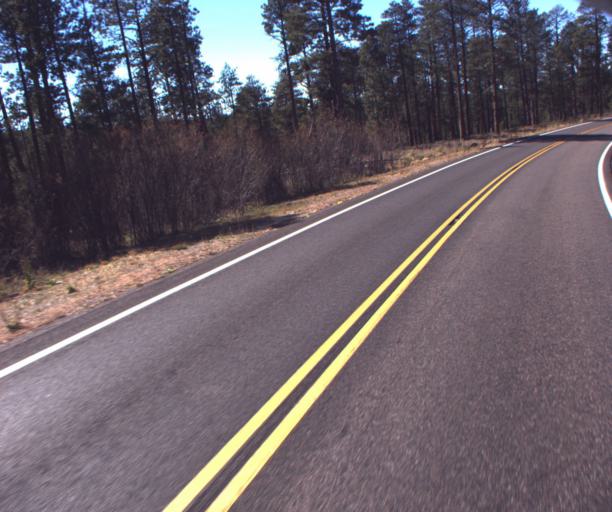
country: US
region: Arizona
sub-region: Coconino County
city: Fredonia
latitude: 36.6672
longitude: -112.1988
